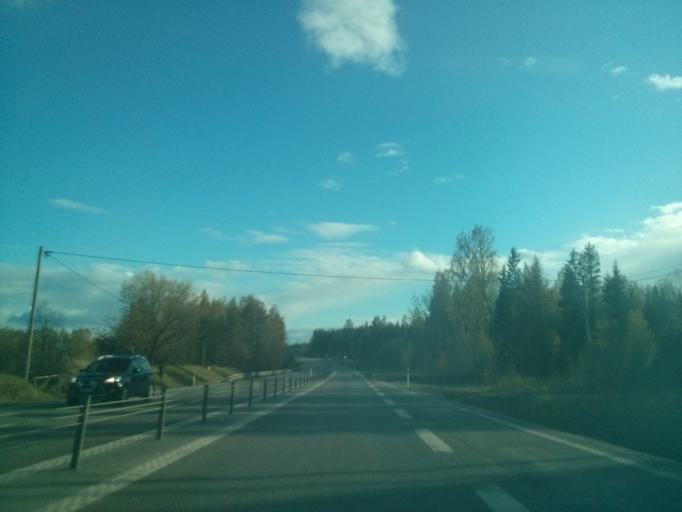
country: SE
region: Vaesternorrland
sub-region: Sundsvalls Kommun
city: Njurundabommen
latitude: 62.1575
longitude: 17.3520
